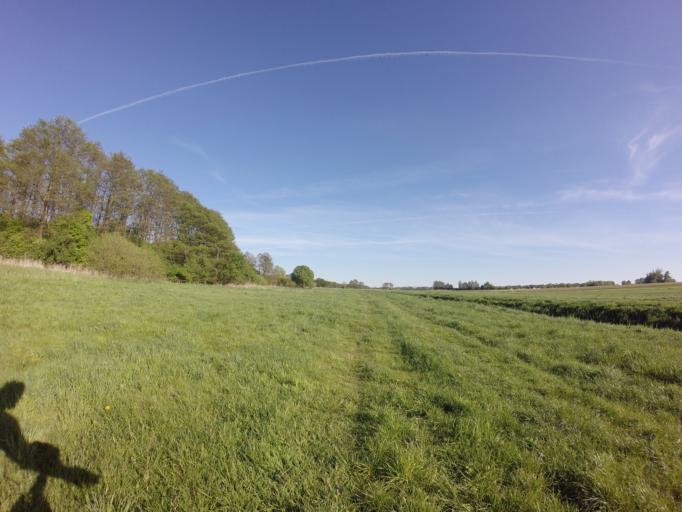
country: PL
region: West Pomeranian Voivodeship
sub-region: Powiat choszczenski
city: Pelczyce
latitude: 53.1306
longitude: 15.3243
